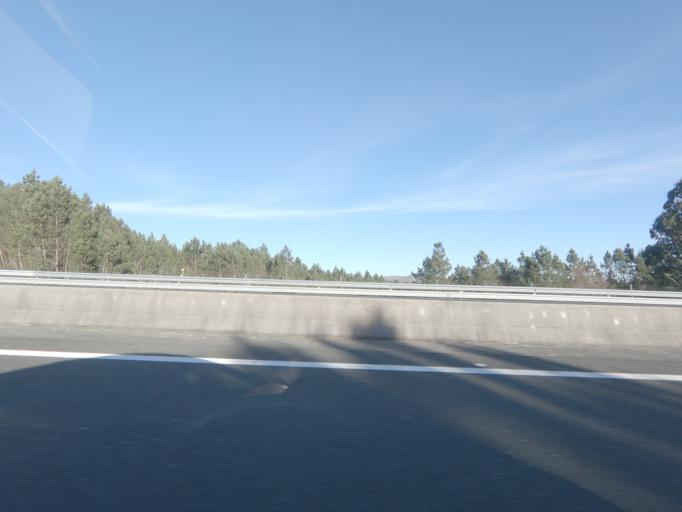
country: ES
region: Galicia
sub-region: Provincia de Ourense
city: Pinor
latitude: 42.5341
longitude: -8.0145
